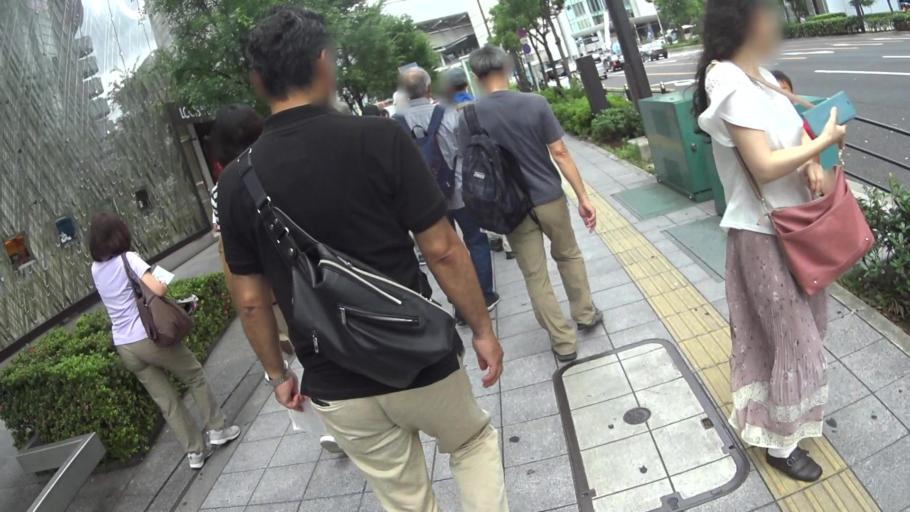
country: JP
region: Osaka
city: Osaka-shi
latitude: 34.6996
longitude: 135.4957
